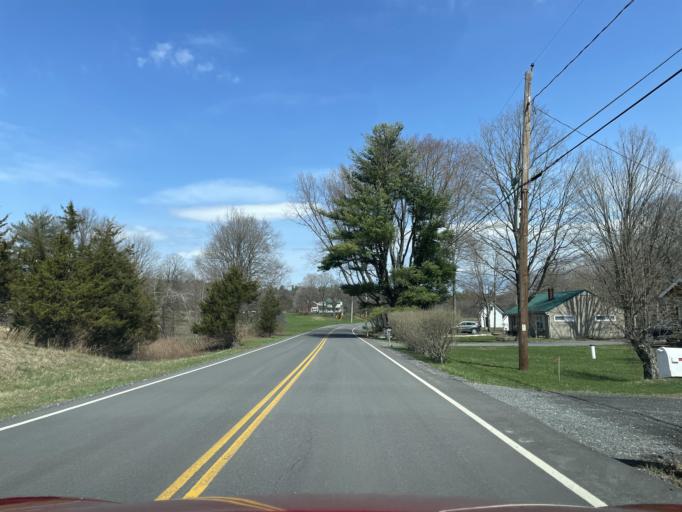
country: US
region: New York
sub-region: Ulster County
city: Manorville
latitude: 42.1352
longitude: -74.0153
